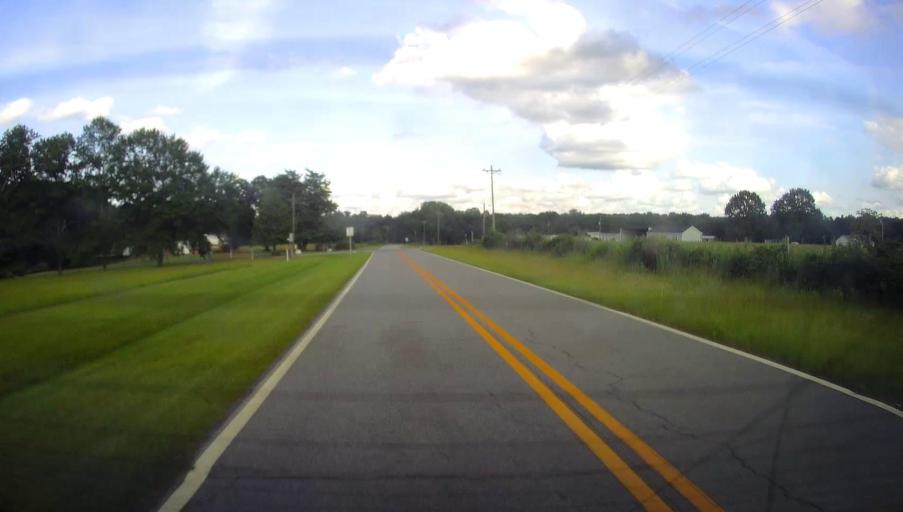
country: US
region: Georgia
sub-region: Crawford County
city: Knoxville
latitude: 32.7556
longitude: -83.9201
